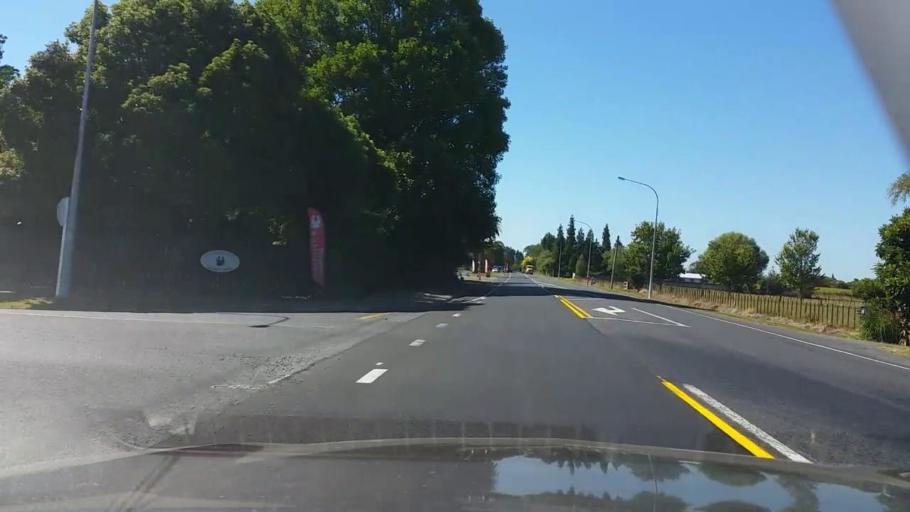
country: NZ
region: Waikato
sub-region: Hamilton City
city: Hamilton
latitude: -37.6703
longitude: 175.3051
